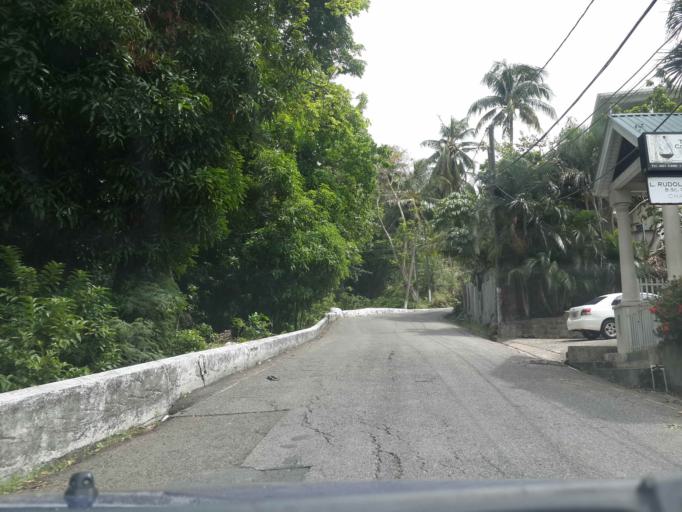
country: LC
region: Castries Quarter
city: Castries
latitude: 14.0069
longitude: -60.9924
